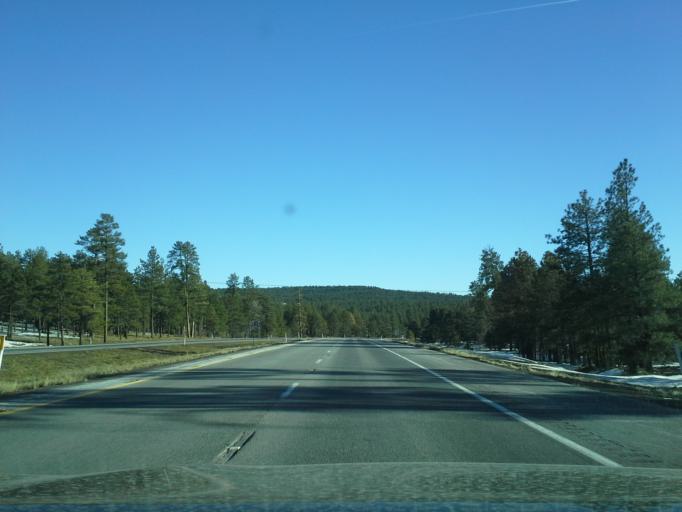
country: US
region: Arizona
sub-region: Coconino County
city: Mountainaire
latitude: 35.0756
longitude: -111.6847
